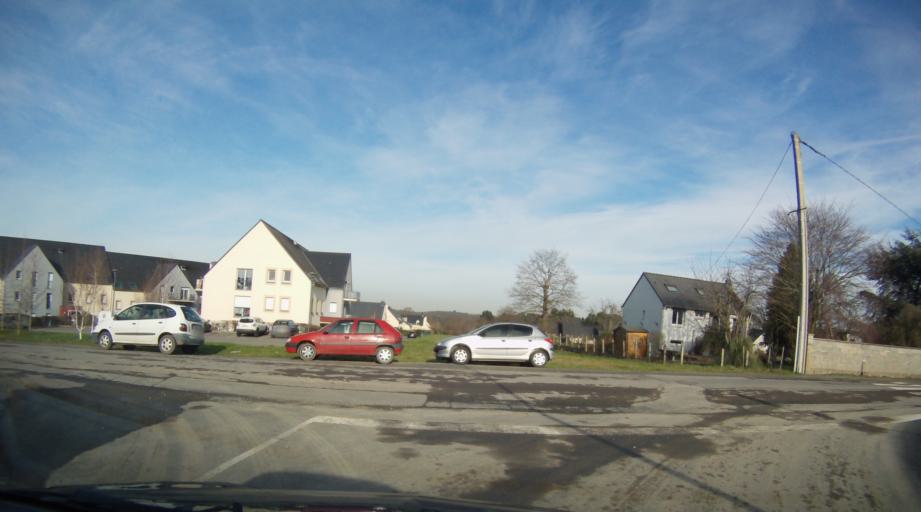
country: FR
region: Brittany
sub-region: Departement d'Ille-et-Vilaine
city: Bourgbarre
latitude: 47.9955
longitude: -1.6215
